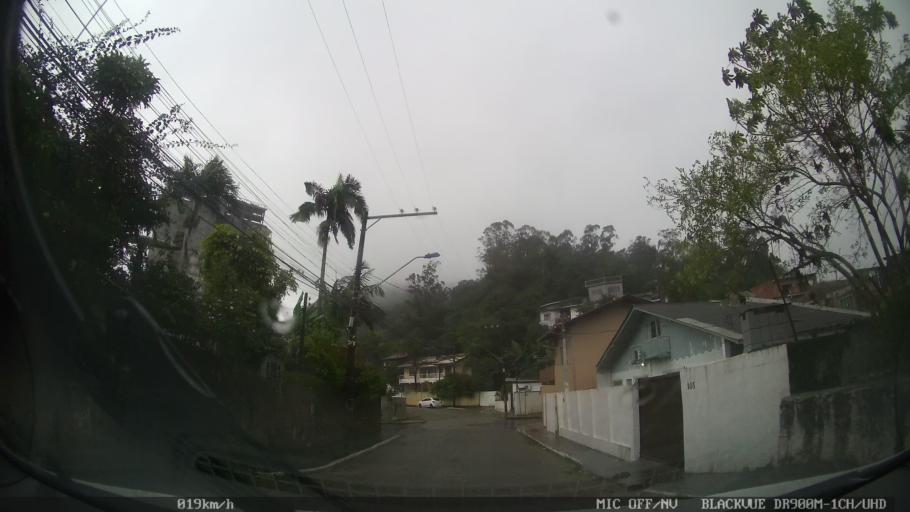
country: BR
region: Santa Catarina
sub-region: Itajai
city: Itajai
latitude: -26.9248
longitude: -48.6478
